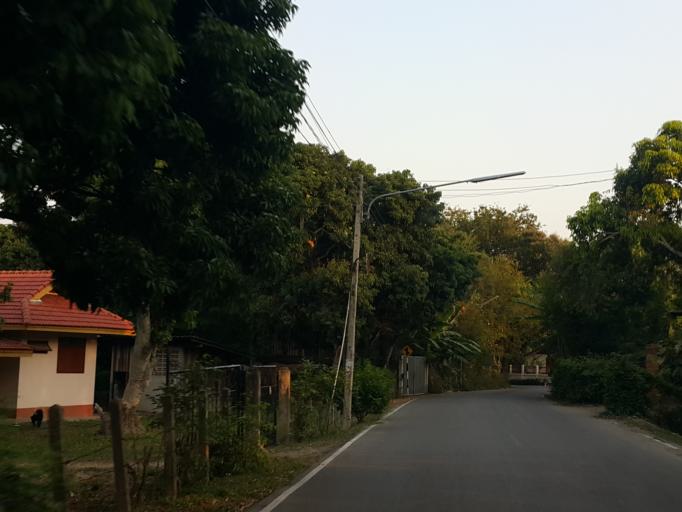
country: TH
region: Chiang Mai
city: San Sai
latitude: 18.8874
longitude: 98.9662
